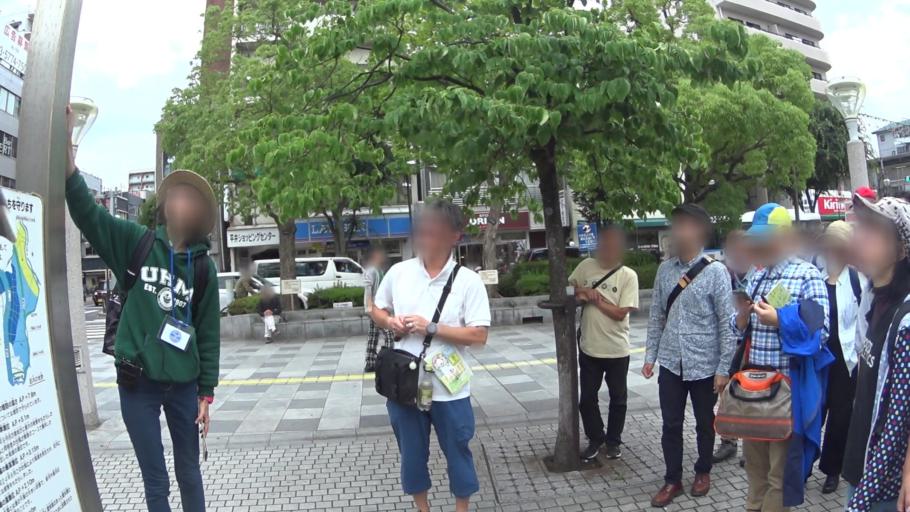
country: JP
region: Tokyo
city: Urayasu
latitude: 35.7072
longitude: 139.8410
